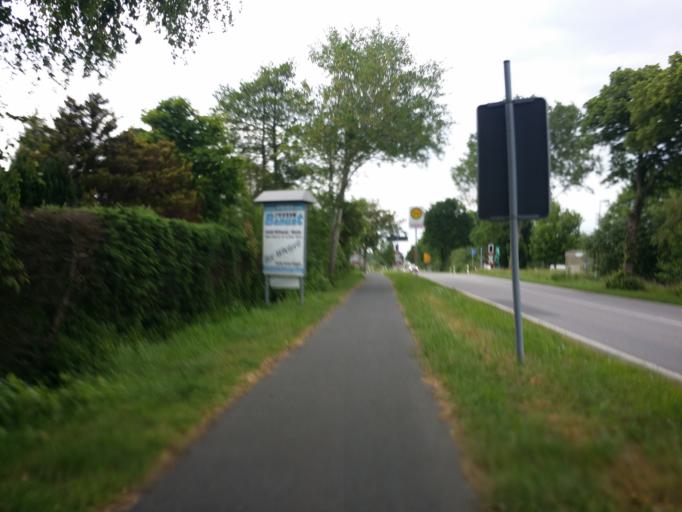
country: DE
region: Lower Saxony
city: Wittmund
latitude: 53.5815
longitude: 7.7814
